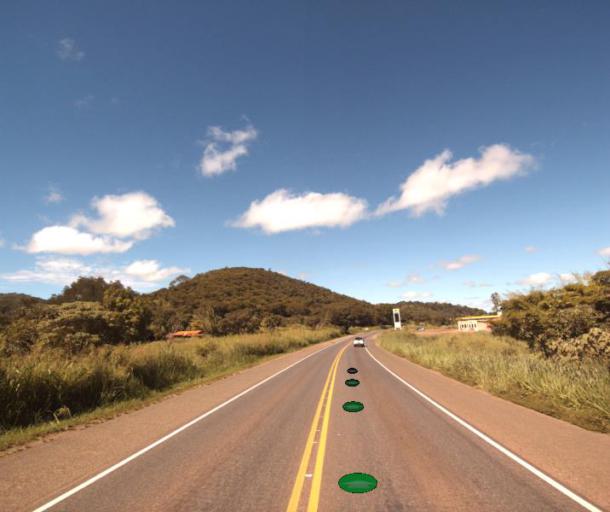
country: BR
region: Goias
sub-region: Rialma
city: Rialma
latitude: -15.2738
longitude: -49.5508
